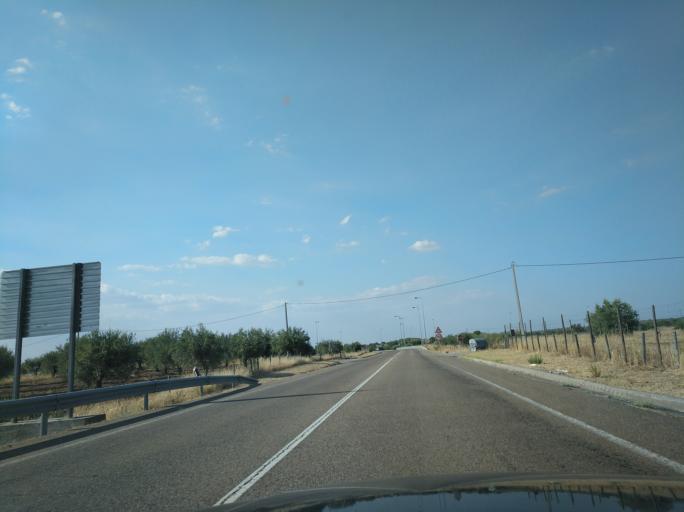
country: PT
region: Evora
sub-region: Mourao
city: Mourao
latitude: 38.3801
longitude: -7.3316
